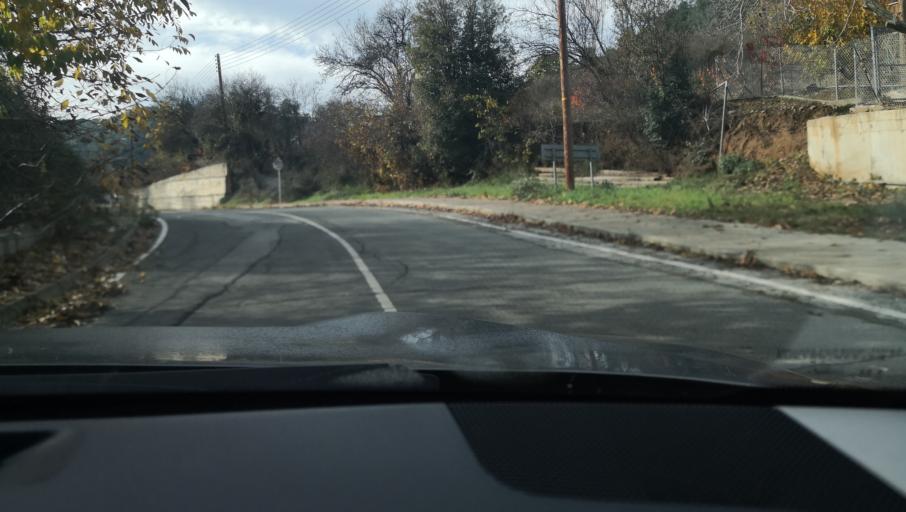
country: CY
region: Lefkosia
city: Lefka
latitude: 35.0319
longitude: 32.7303
